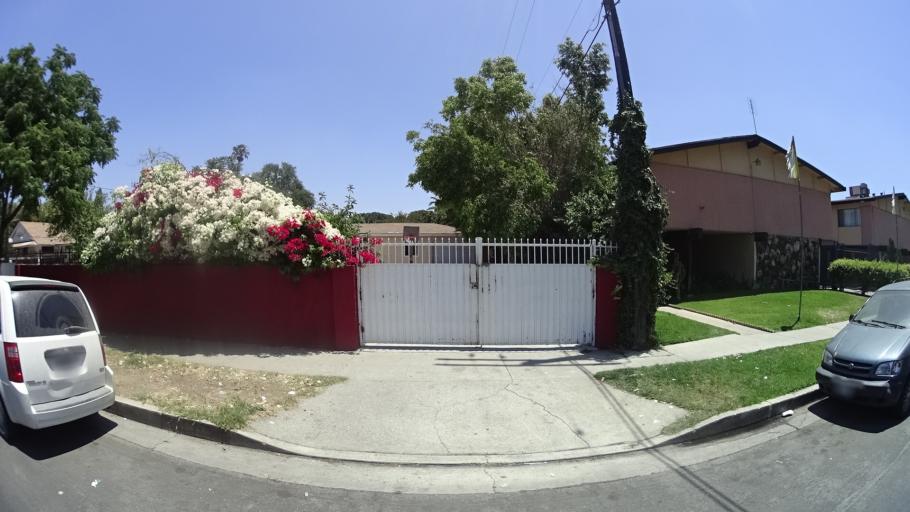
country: US
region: California
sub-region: Los Angeles County
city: Van Nuys
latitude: 34.2289
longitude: -118.4611
